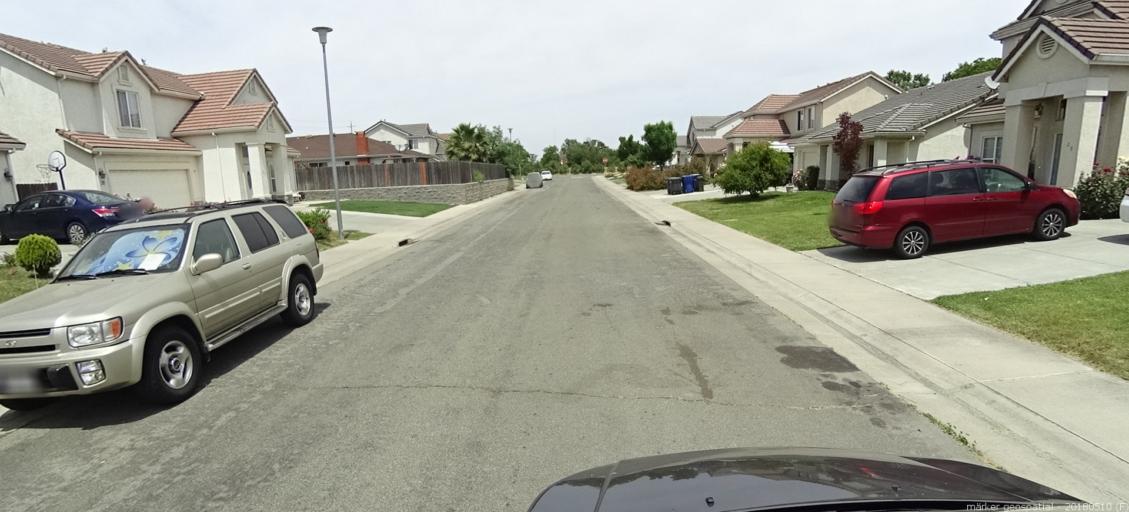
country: US
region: California
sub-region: Sacramento County
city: Rio Linda
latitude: 38.6503
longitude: -121.4564
